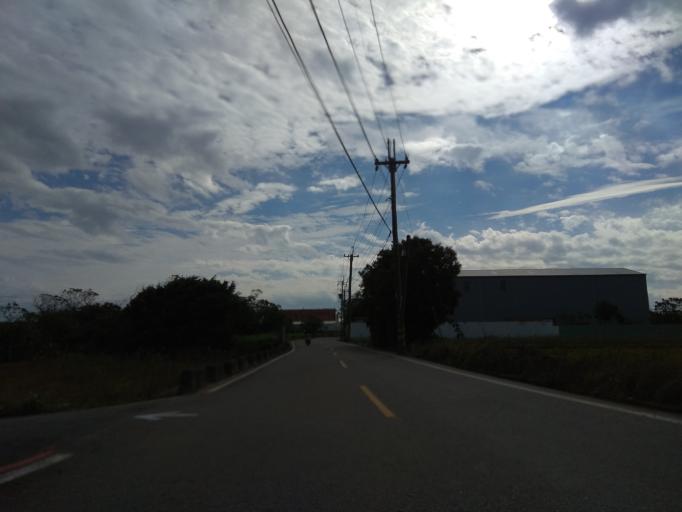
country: TW
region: Taiwan
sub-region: Hsinchu
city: Zhubei
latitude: 24.9575
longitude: 121.1090
